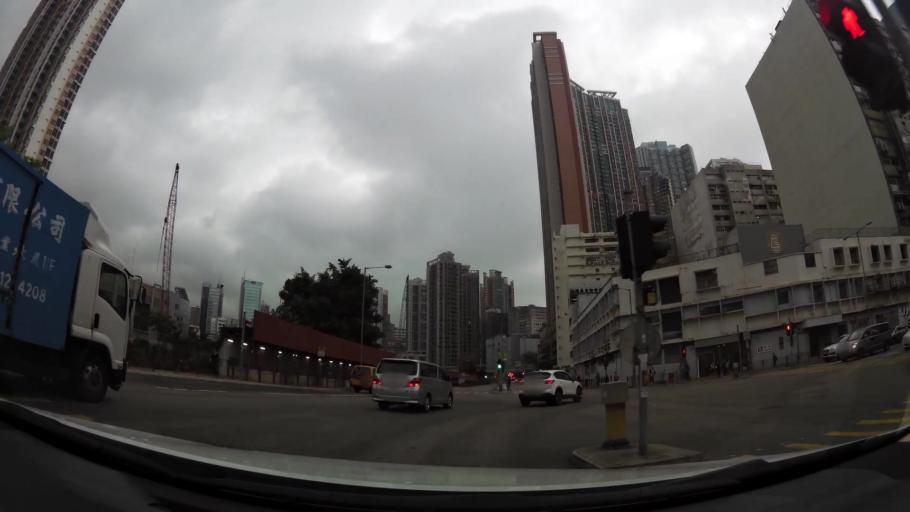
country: HK
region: Tsuen Wan
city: Tsuen Wan
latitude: 22.3664
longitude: 114.1143
